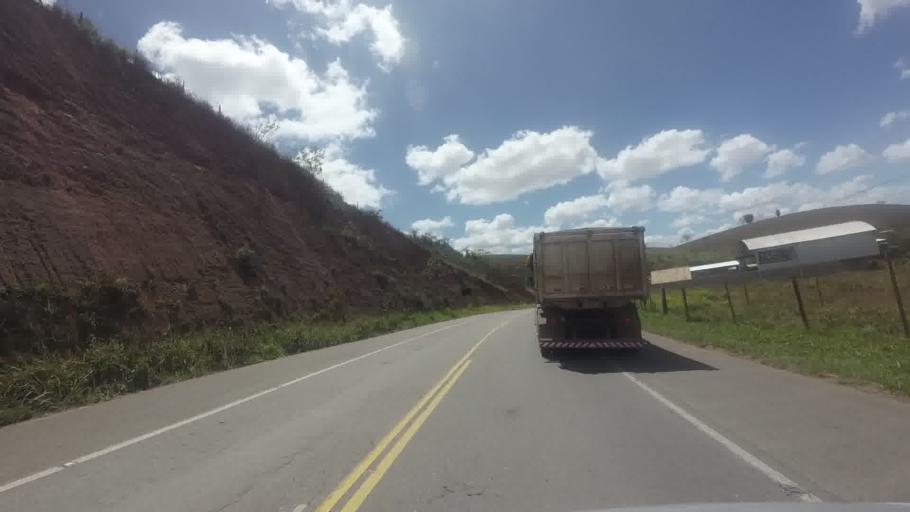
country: BR
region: Rio de Janeiro
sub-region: Santo Antonio De Padua
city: Santo Antonio de Padua
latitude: -21.6571
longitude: -42.3290
